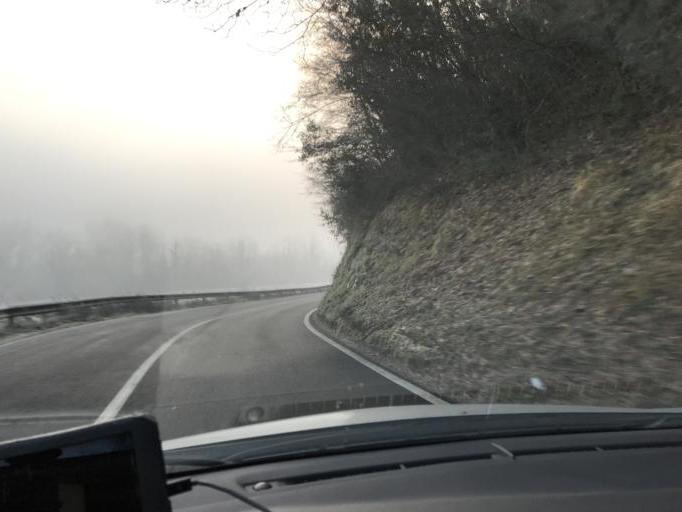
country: IT
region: Latium
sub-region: Provincia di Rieti
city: Colli sul Velino
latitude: 42.5184
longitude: 12.7362
